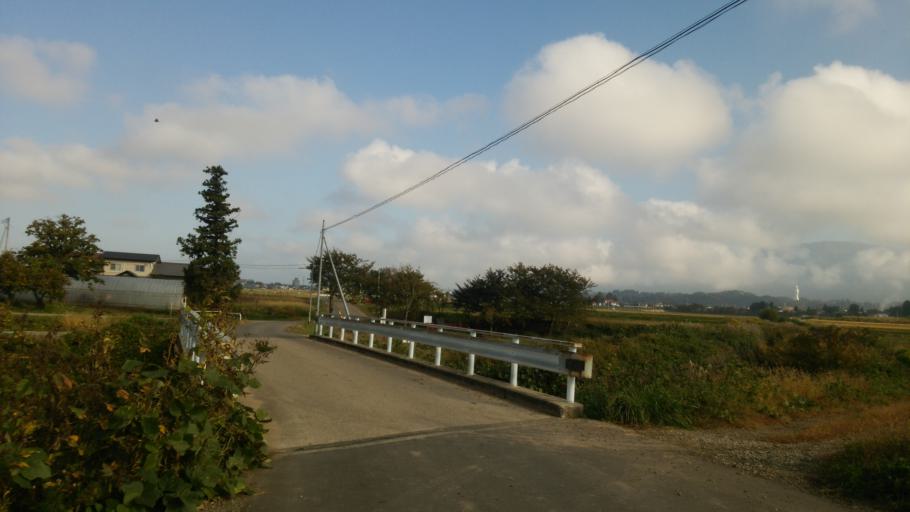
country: JP
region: Fukushima
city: Kitakata
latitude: 37.5320
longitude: 139.9357
